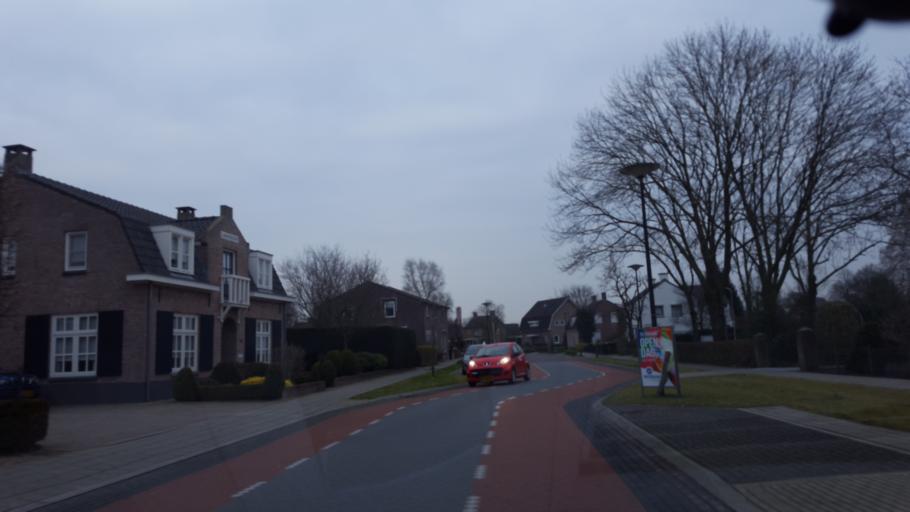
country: NL
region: North Brabant
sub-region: Gemeente Asten
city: Asten
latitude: 51.4441
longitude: 5.7623
